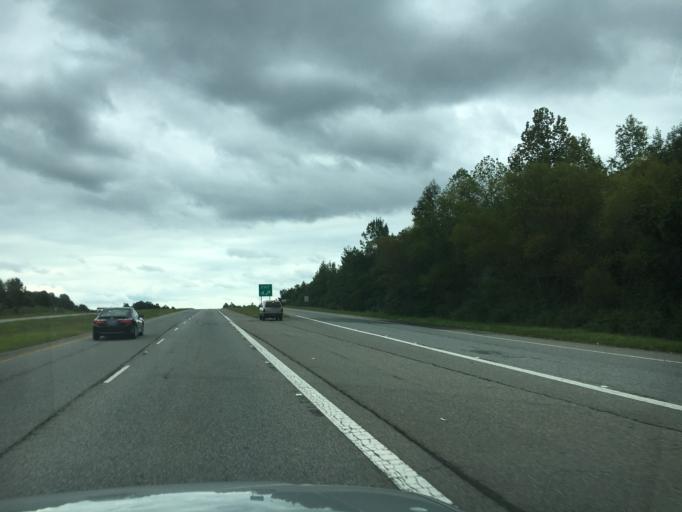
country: US
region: South Carolina
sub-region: Greenville County
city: Mauldin
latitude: 34.7211
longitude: -82.3479
